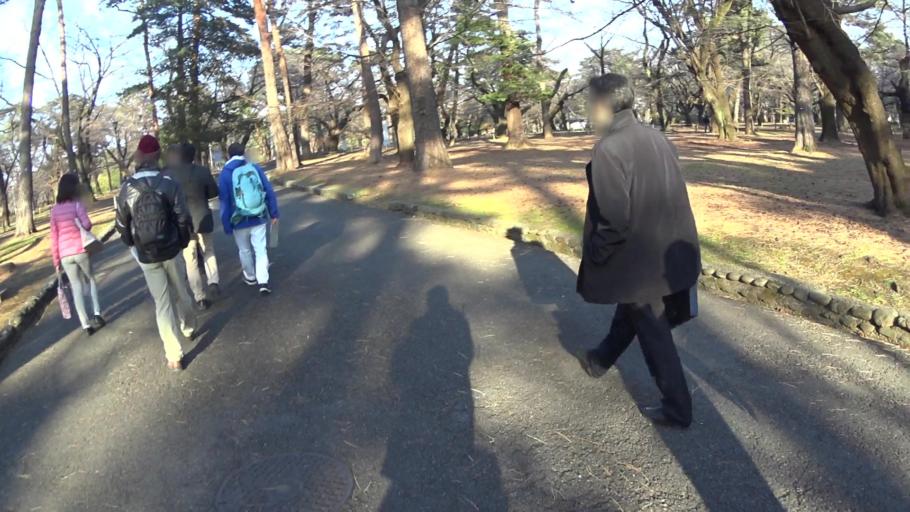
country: JP
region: Saitama
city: Saitama
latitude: 35.9182
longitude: 139.6290
